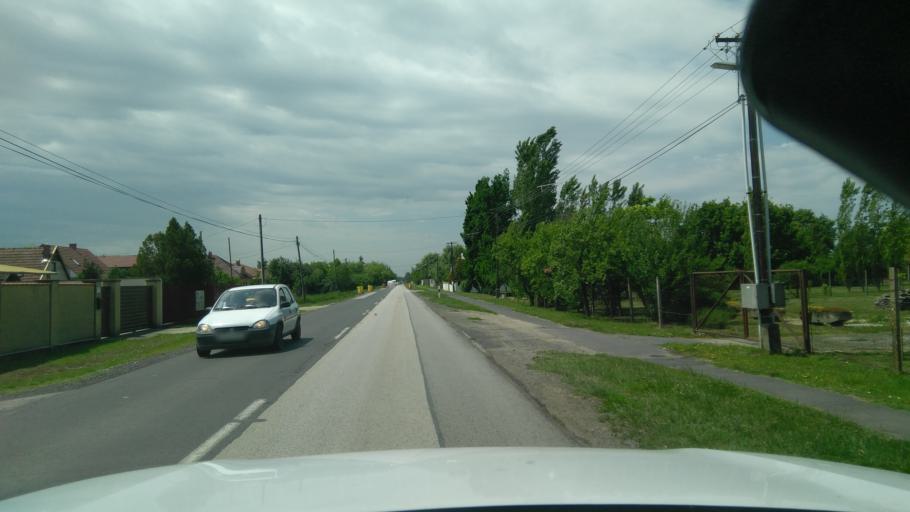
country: HU
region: Bekes
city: Bekescsaba
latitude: 46.6977
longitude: 21.1376
